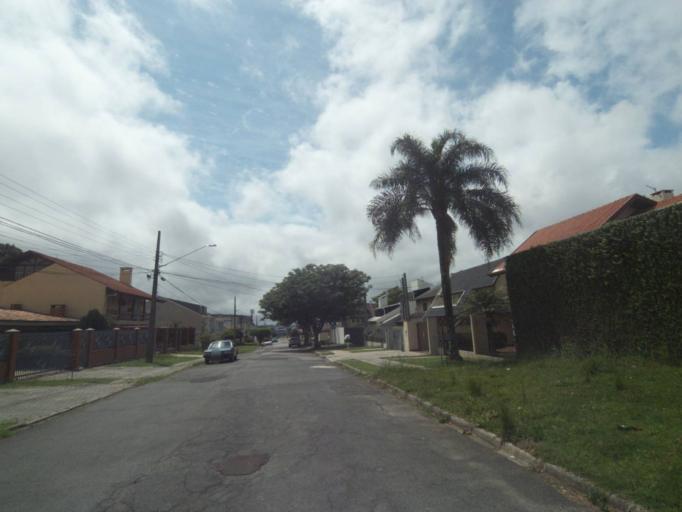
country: BR
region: Parana
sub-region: Pinhais
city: Pinhais
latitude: -25.4317
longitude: -49.2256
